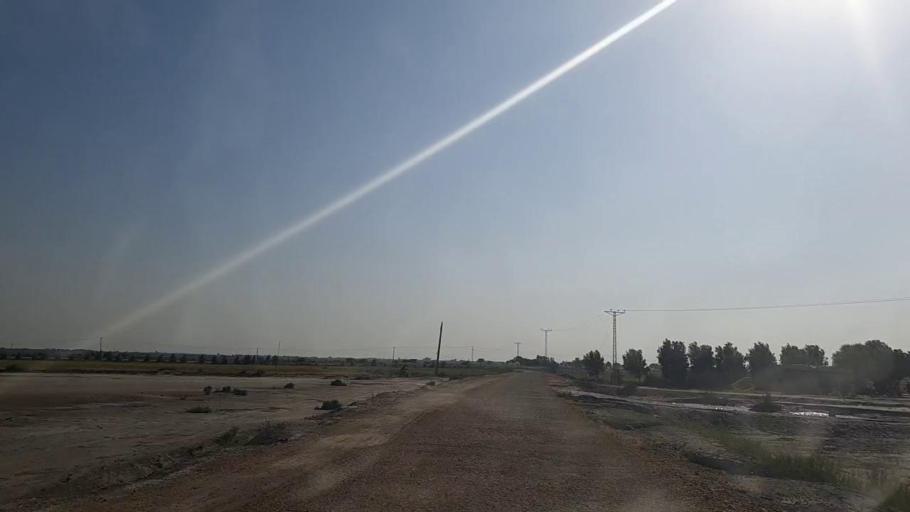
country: PK
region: Sindh
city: Mirpur Batoro
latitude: 24.5926
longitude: 68.1705
